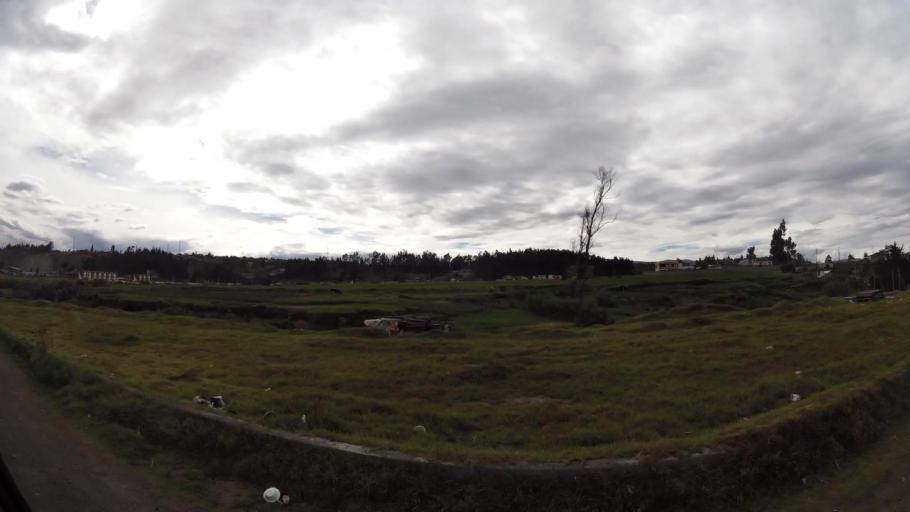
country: EC
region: Cotopaxi
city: Latacunga
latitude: -0.9484
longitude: -78.6171
